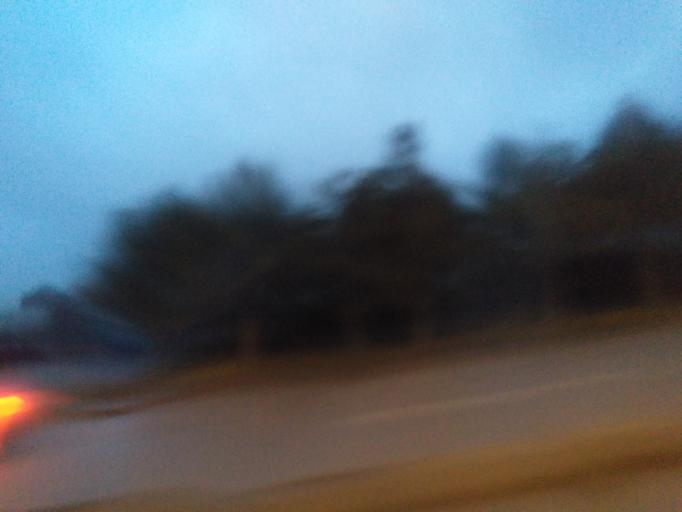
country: TR
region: Ankara
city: Ankara
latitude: 39.9591
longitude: 32.8231
